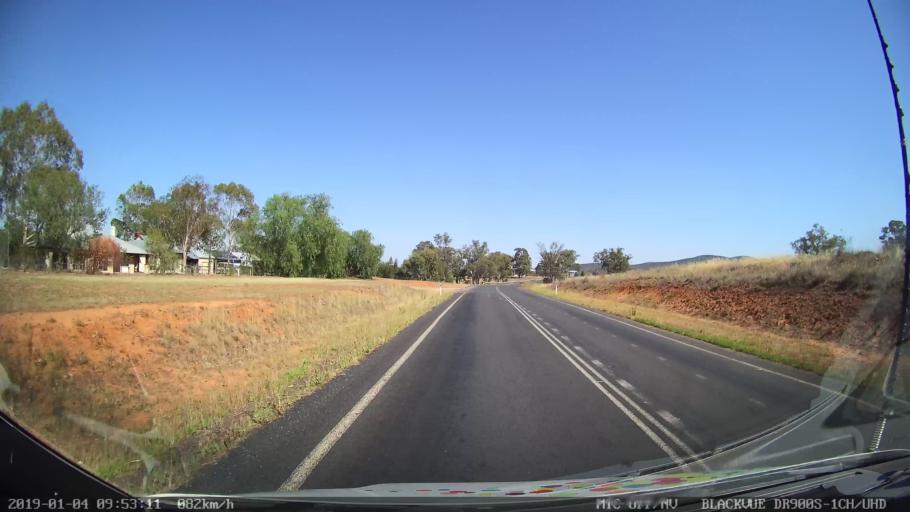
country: AU
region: New South Wales
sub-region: Cabonne
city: Canowindra
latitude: -33.5553
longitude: 148.4218
